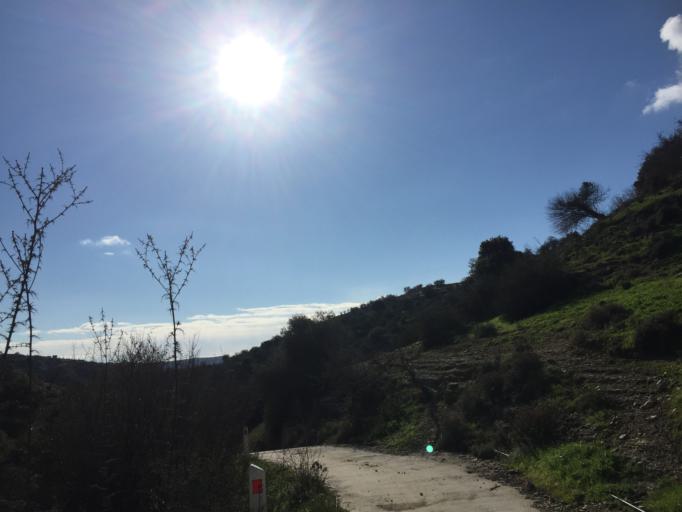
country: CY
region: Pafos
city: Mesogi
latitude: 34.8339
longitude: 32.5129
